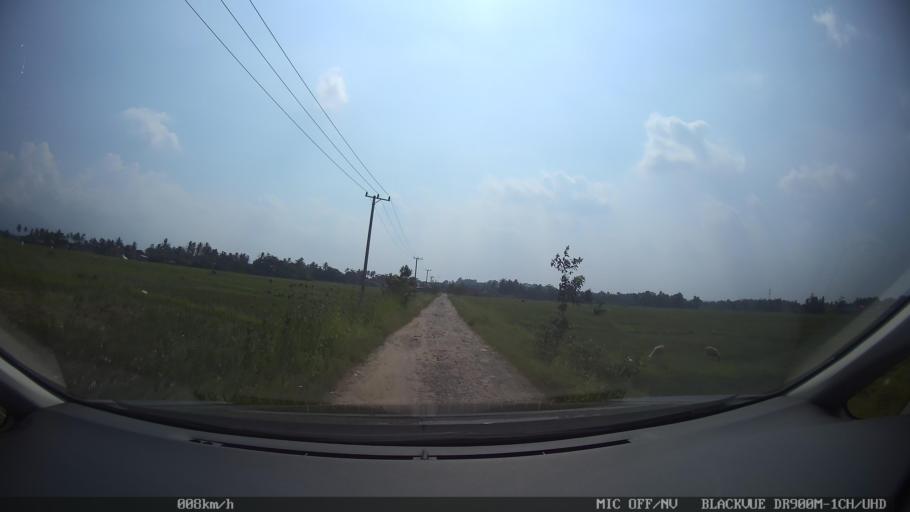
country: ID
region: Lampung
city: Natar
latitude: -5.2951
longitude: 105.2336
